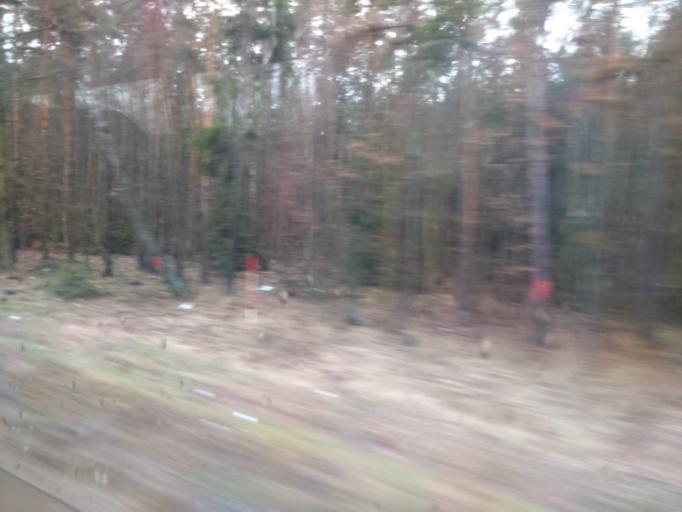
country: CZ
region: Plzensky
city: Vejprnice
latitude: 49.7199
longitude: 13.2992
